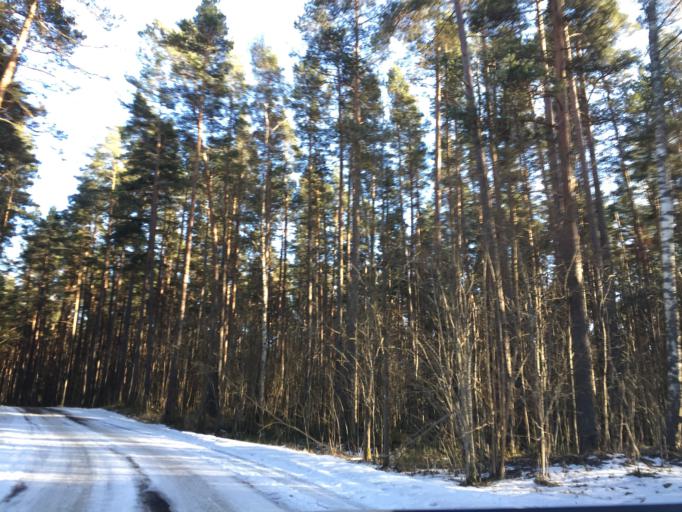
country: LV
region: Babite
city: Pinki
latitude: 56.9329
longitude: 23.9061
